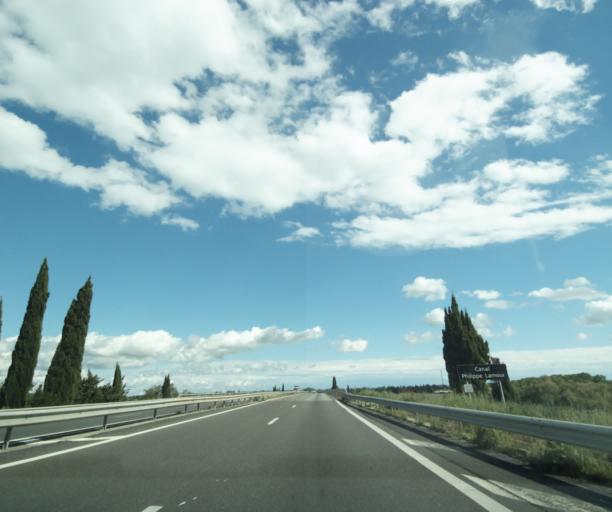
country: FR
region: Languedoc-Roussillon
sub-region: Departement du Gard
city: Bellegarde
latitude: 43.7268
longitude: 4.5016
